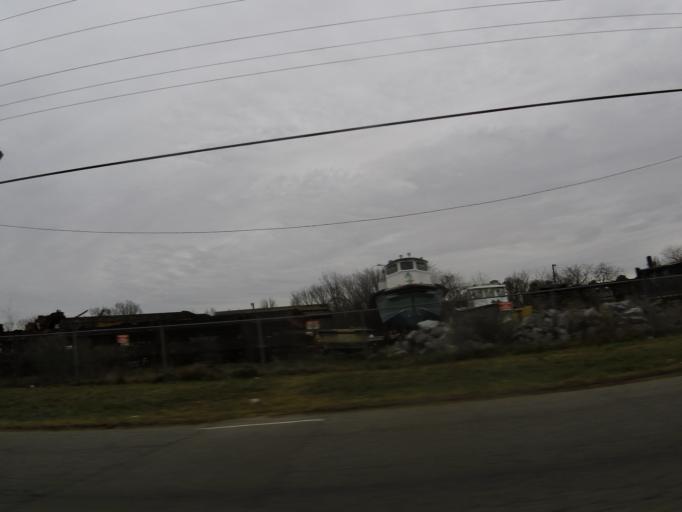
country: US
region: Virginia
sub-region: City of Portsmouth
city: Portsmouth
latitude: 36.8479
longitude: -76.3258
